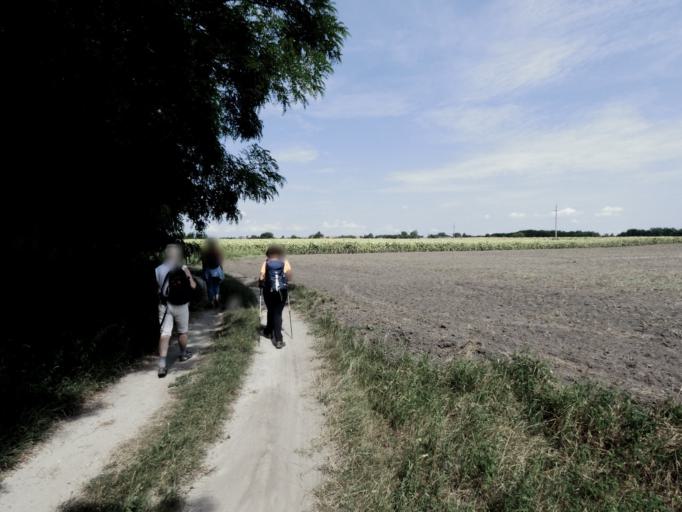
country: HU
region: Pest
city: Danszentmiklos
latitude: 47.1632
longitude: 19.5056
